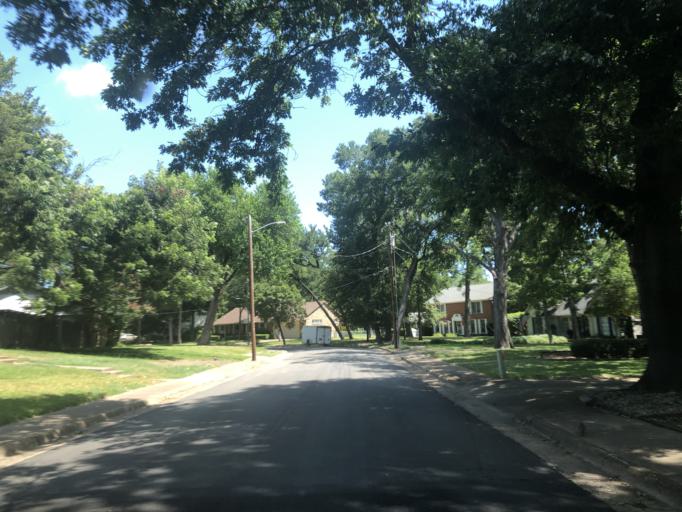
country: US
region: Texas
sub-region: Dallas County
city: Duncanville
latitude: 32.6495
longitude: -96.9197
